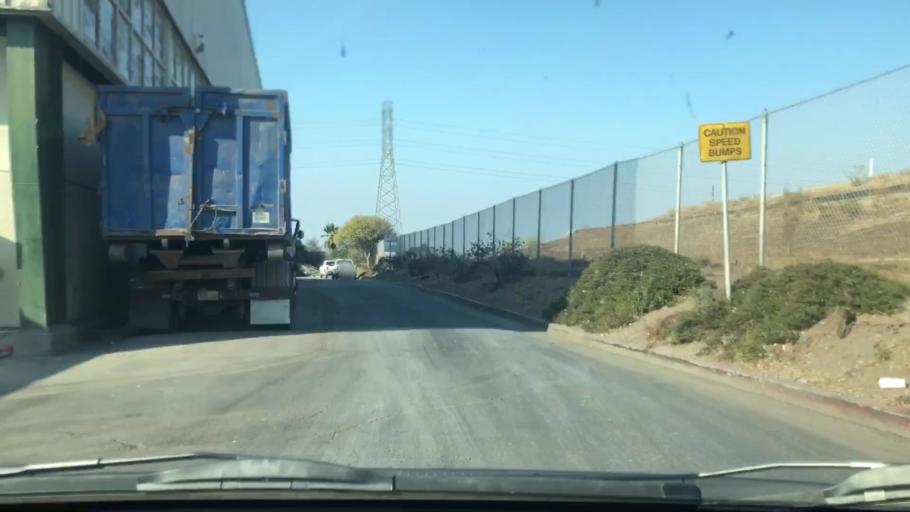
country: US
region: California
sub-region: Santa Clara County
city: Sunnyvale
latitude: 37.4177
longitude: -122.0104
